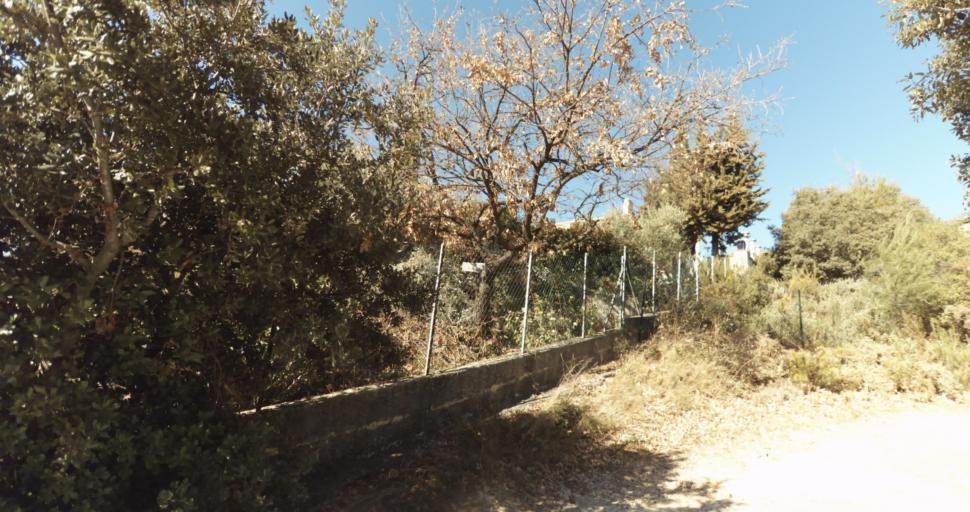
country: FR
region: Provence-Alpes-Cote d'Azur
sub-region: Departement des Bouches-du-Rhone
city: Peypin
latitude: 43.3868
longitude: 5.5620
